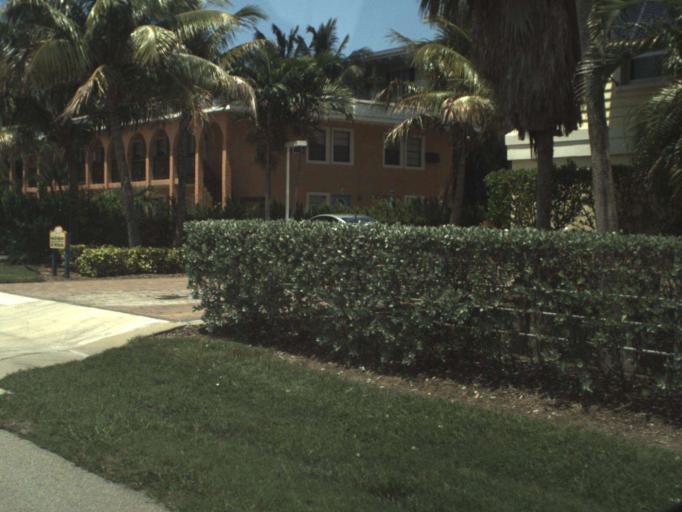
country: US
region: Florida
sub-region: Brevard County
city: Indialantic
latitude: 28.0886
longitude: -80.5657
